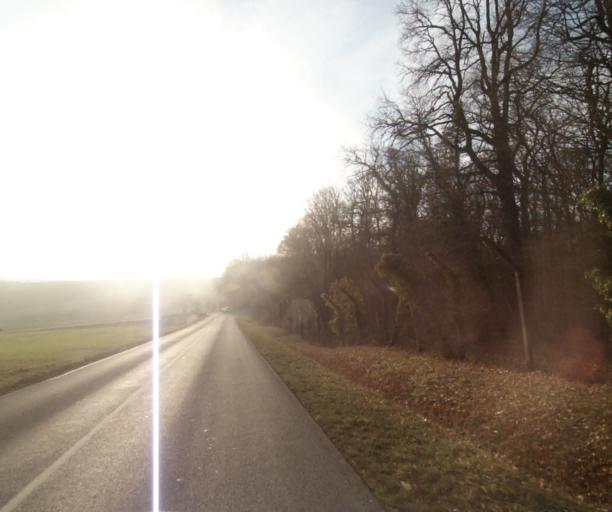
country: FR
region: Champagne-Ardenne
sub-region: Departement de la Haute-Marne
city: Chancenay
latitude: 48.7160
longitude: 4.9454
